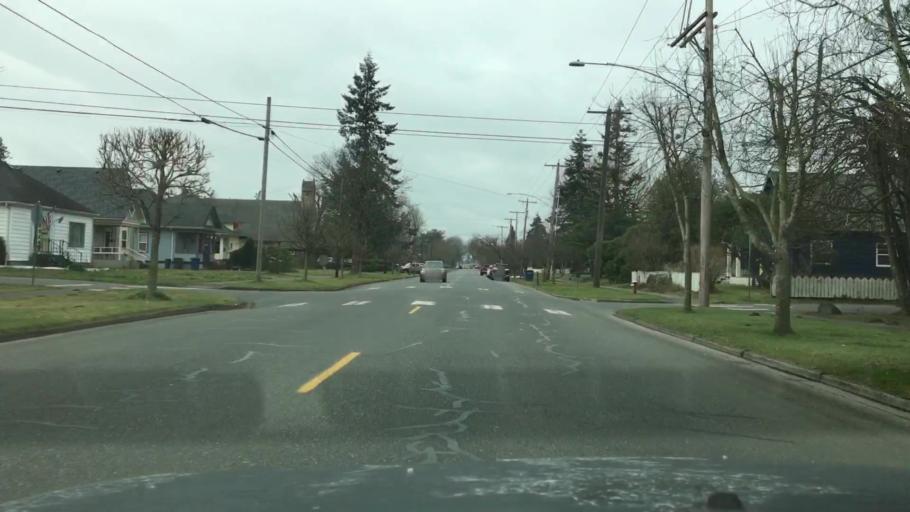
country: US
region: Washington
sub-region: Skagit County
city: Sedro-Woolley
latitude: 48.5054
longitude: -122.2282
